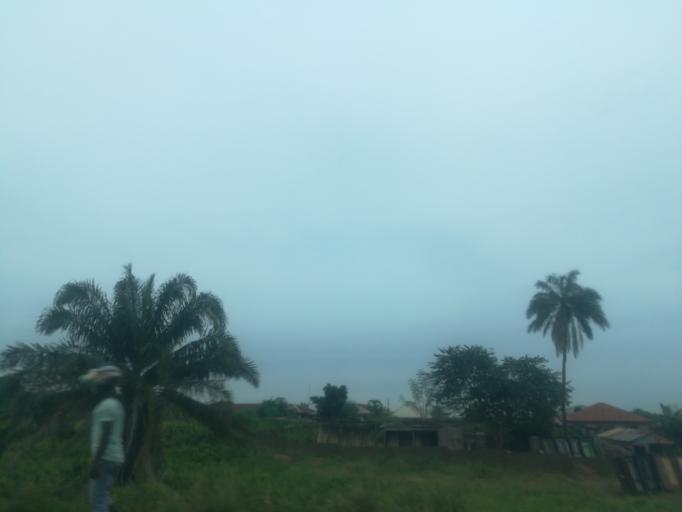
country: NG
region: Oyo
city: Egbeda
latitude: 7.3814
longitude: 4.0020
